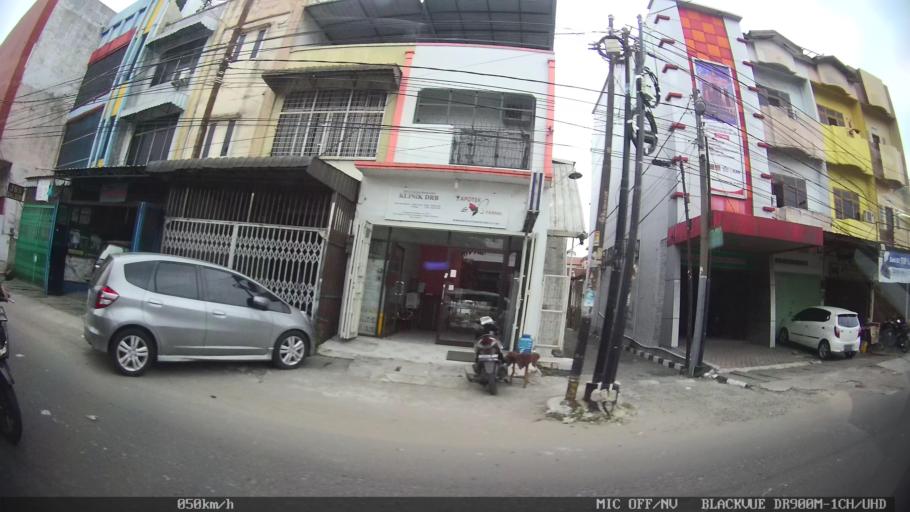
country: ID
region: North Sumatra
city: Medan
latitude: 3.5686
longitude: 98.6872
